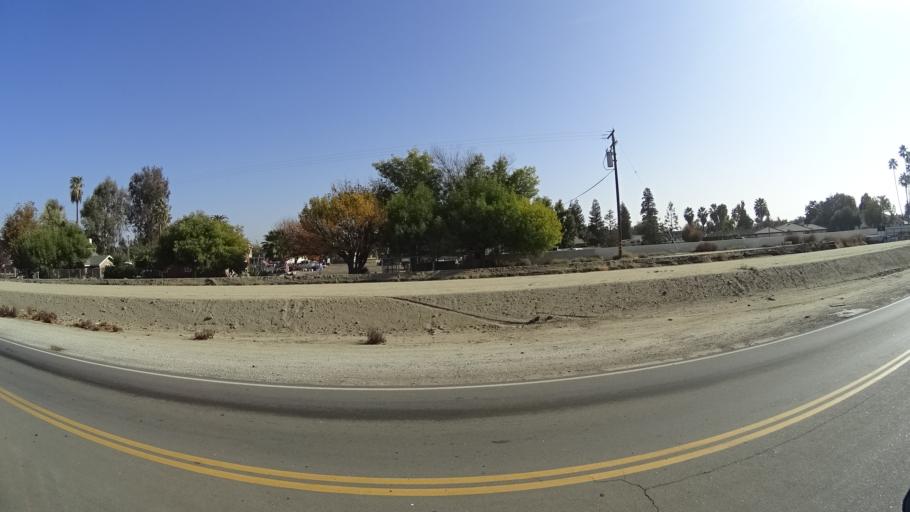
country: US
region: California
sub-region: Kern County
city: Greenfield
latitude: 35.2731
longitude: -119.0214
